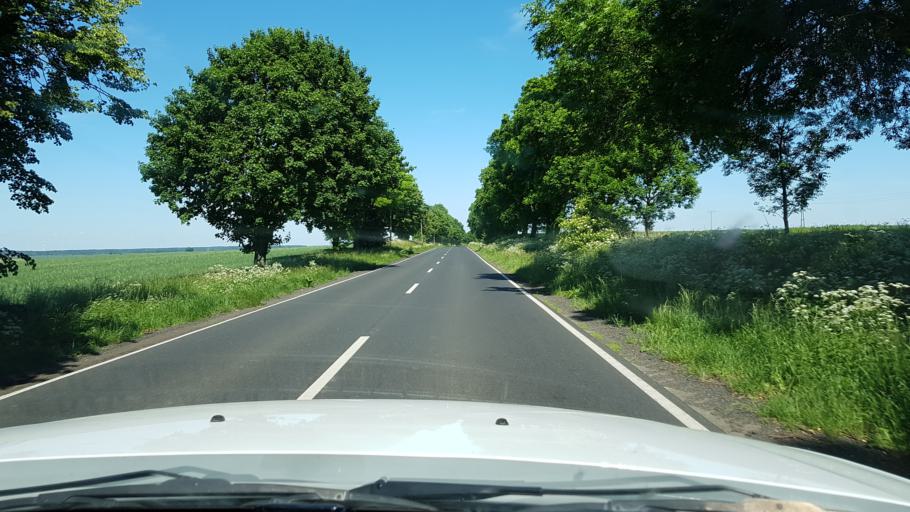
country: PL
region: West Pomeranian Voivodeship
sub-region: Powiat gryfinski
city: Banie
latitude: 53.1080
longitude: 14.6920
